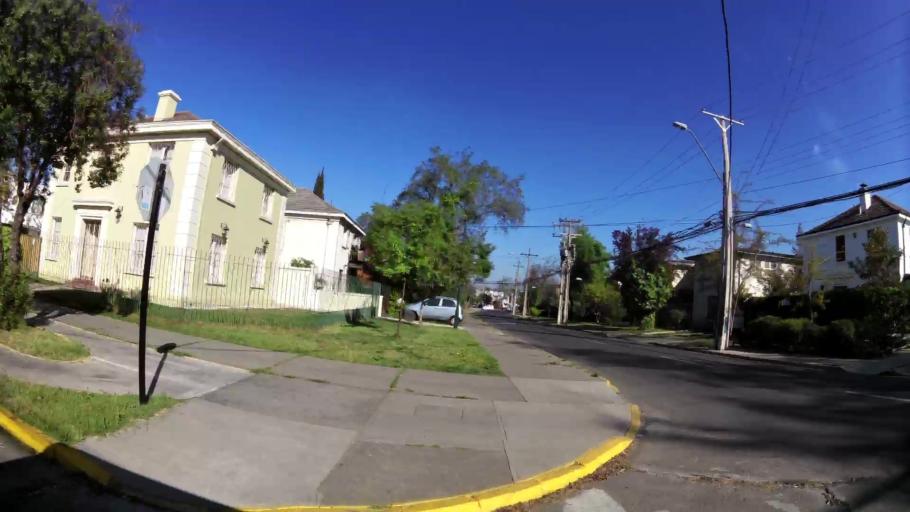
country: CL
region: Santiago Metropolitan
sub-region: Provincia de Santiago
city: Villa Presidente Frei, Nunoa, Santiago, Chile
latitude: -33.4448
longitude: -70.5846
